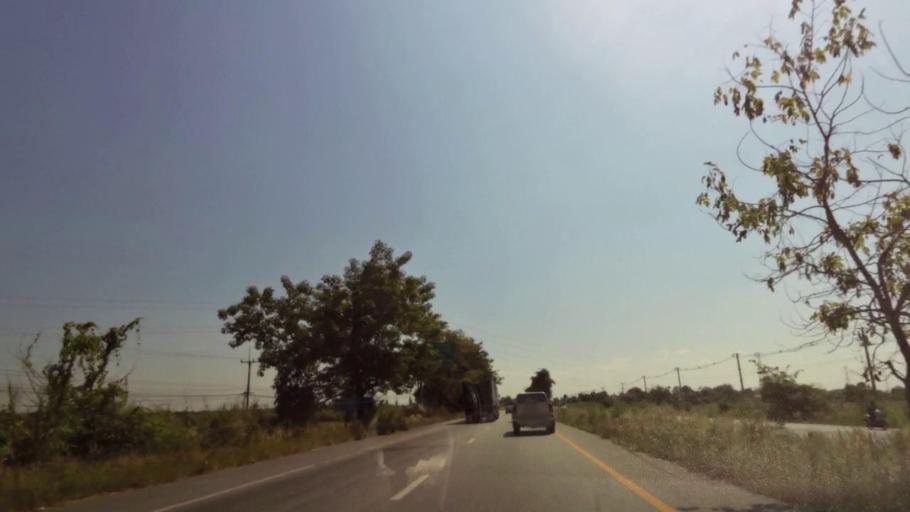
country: TH
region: Nakhon Sawan
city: Kao Liao
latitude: 15.8307
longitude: 100.1184
